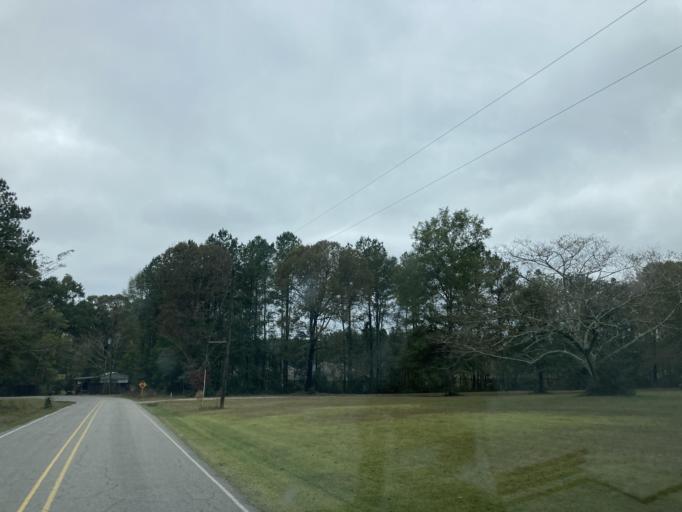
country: US
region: Mississippi
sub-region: Lamar County
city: Purvis
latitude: 31.1775
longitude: -89.4190
